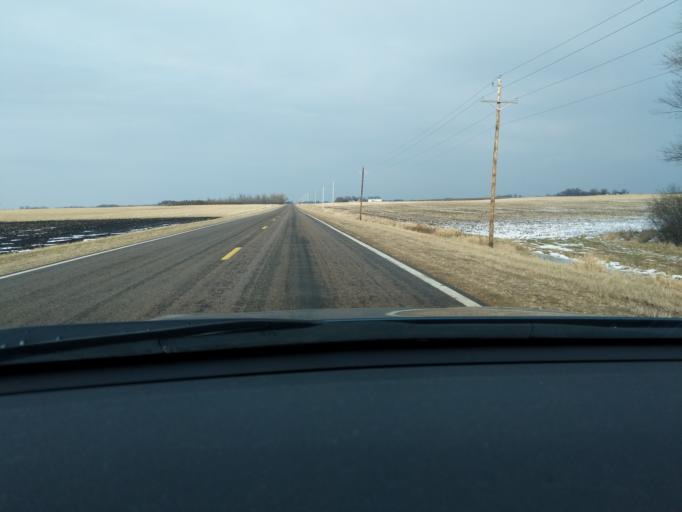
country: US
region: Minnesota
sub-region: Renville County
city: Renville
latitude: 44.7461
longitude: -95.3408
